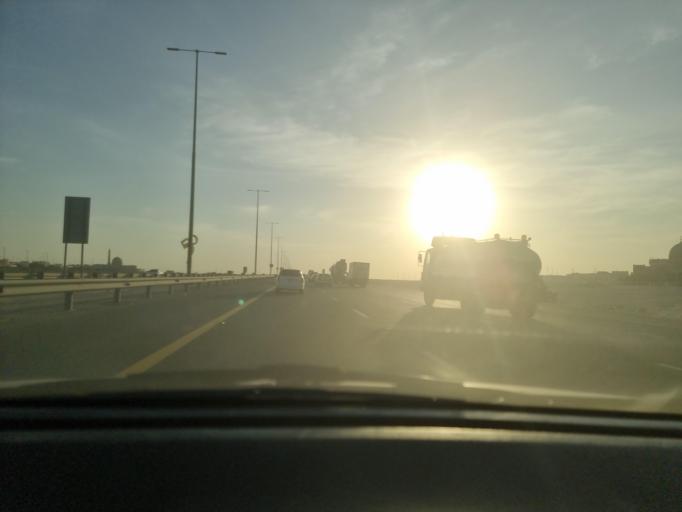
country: AE
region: Abu Dhabi
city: Abu Dhabi
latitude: 24.3323
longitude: 54.6949
